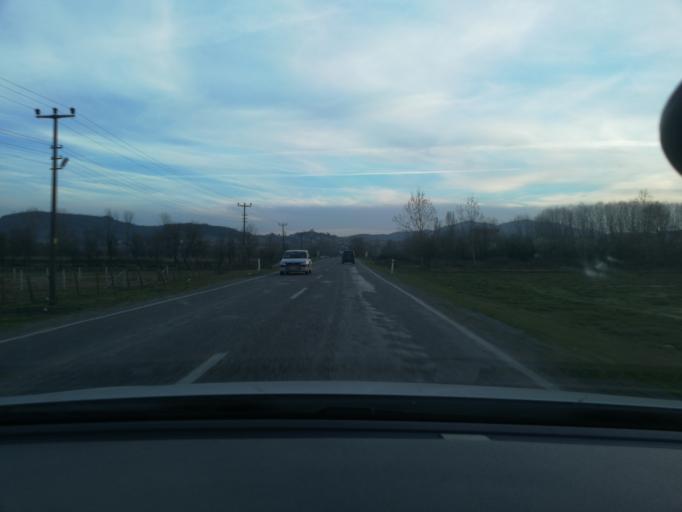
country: TR
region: Zonguldak
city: Saltukova
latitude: 41.5101
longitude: 32.1018
